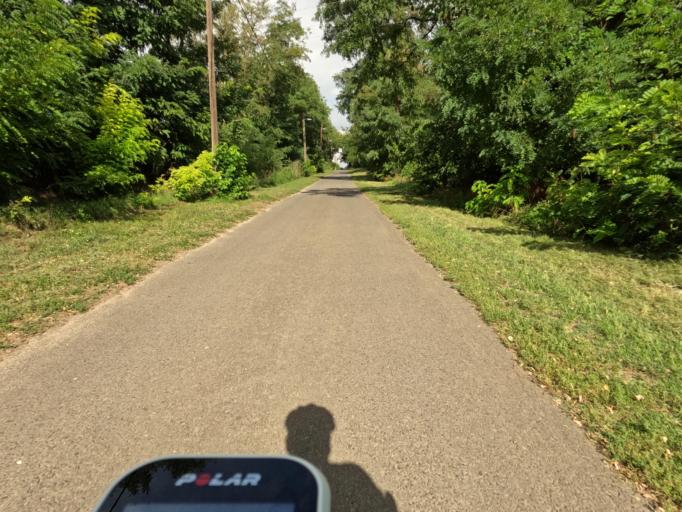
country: HU
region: Tolna
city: Tengelic
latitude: 46.5173
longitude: 18.6973
